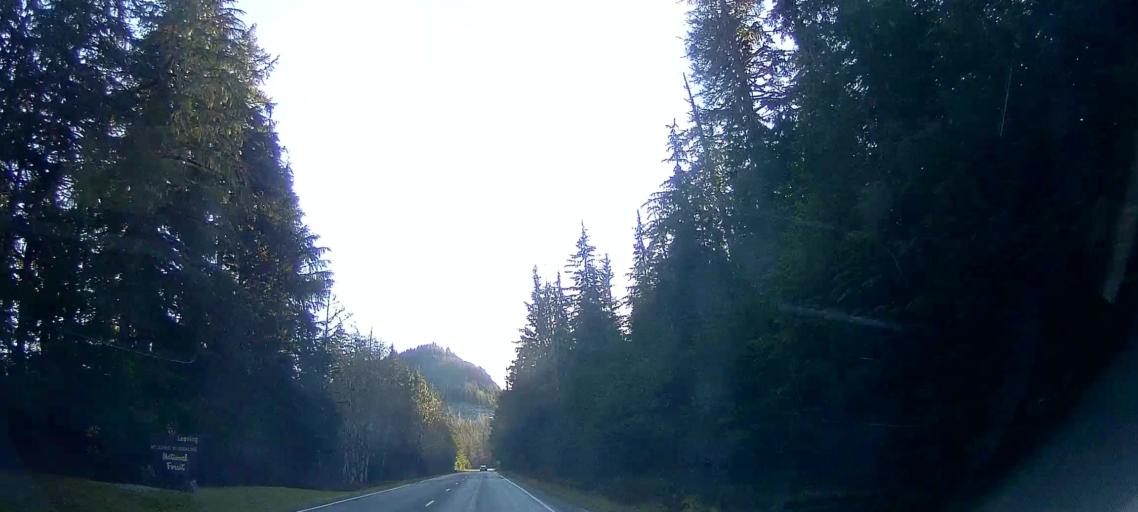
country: US
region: Washington
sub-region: Snohomish County
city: Darrington
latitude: 48.6455
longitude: -121.7295
